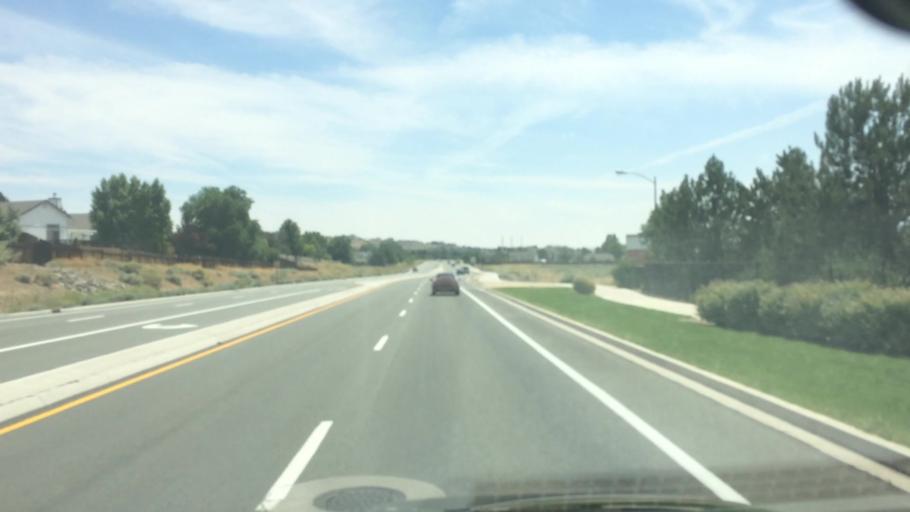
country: US
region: Nevada
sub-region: Washoe County
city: Spanish Springs
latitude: 39.5932
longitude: -119.7147
